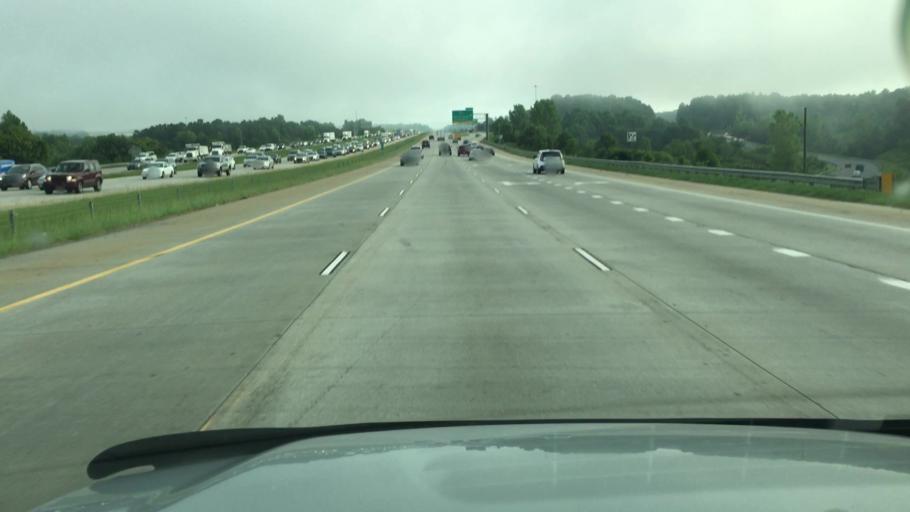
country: US
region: North Carolina
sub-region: Gaston County
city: Belmont
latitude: 35.2331
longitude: -80.9702
